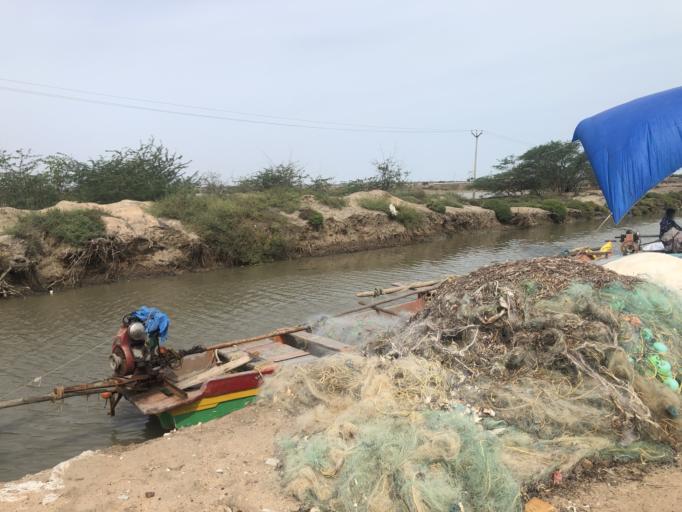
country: IN
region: Tamil Nadu
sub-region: Thanjavur
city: Adirampattinam
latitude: 10.3221
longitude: 79.3788
